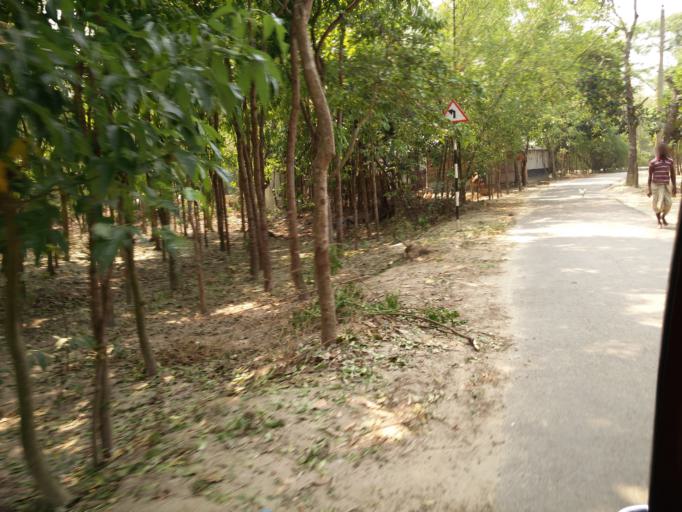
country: BD
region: Dhaka
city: Muktagacha
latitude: 24.8997
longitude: 90.2593
